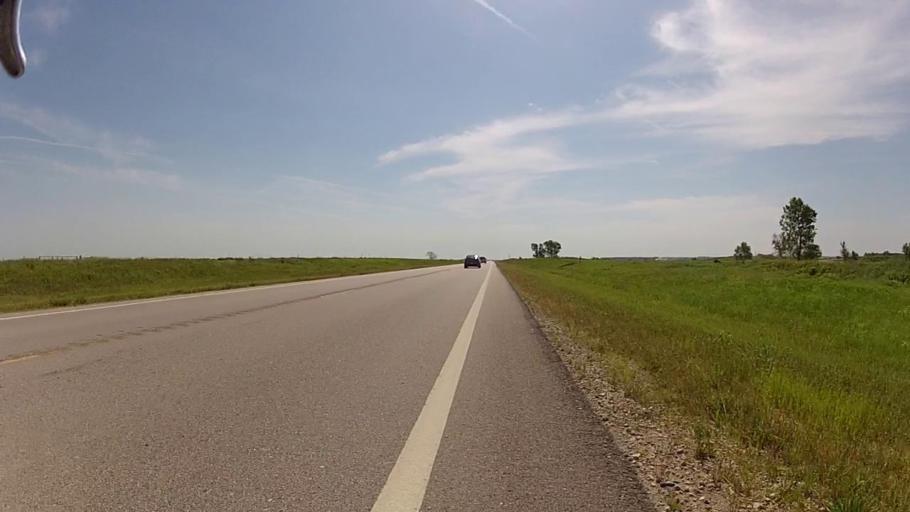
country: US
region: Kansas
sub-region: Cowley County
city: Winfield
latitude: 37.1109
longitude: -96.6161
